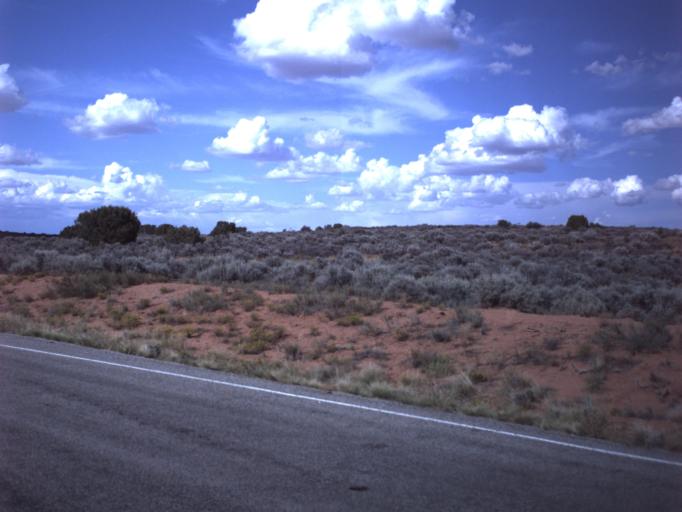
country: US
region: Utah
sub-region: Grand County
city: Moab
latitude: 38.5167
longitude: -109.7300
